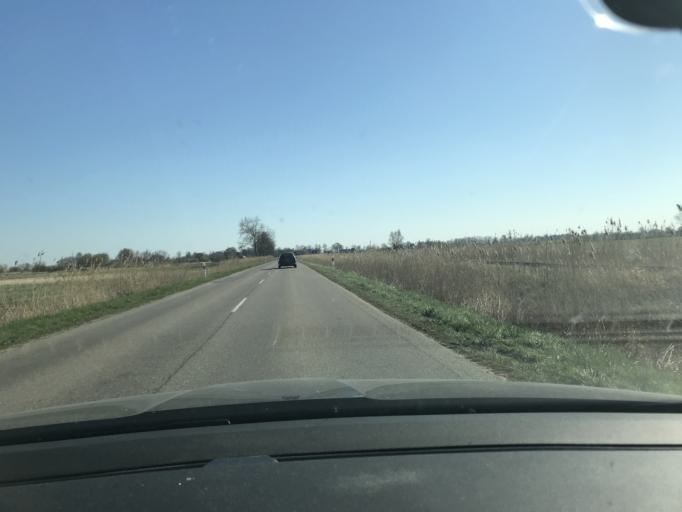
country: PL
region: Pomeranian Voivodeship
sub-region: Powiat nowodworski
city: Nowy Dwor Gdanski
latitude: 54.2513
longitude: 19.1399
